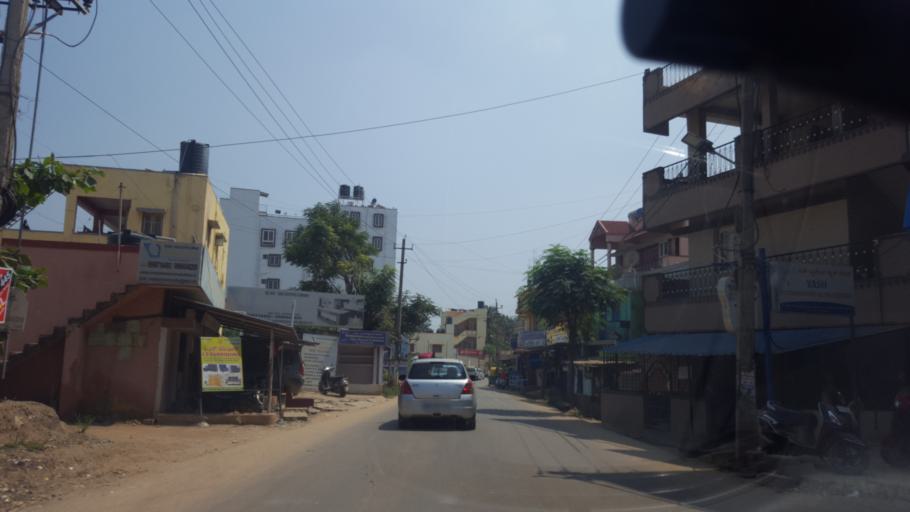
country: IN
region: Karnataka
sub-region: Bangalore Urban
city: Bangalore
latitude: 12.9366
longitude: 77.7048
